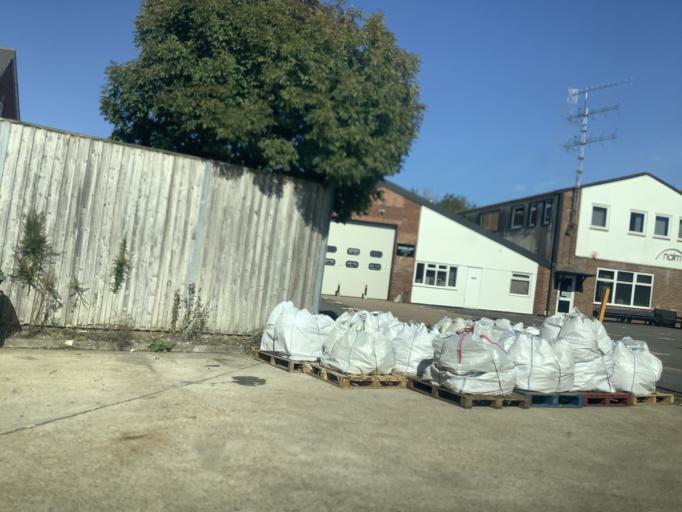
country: GB
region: England
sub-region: Wiltshire
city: Salisbury
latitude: 51.0643
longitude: -1.7814
